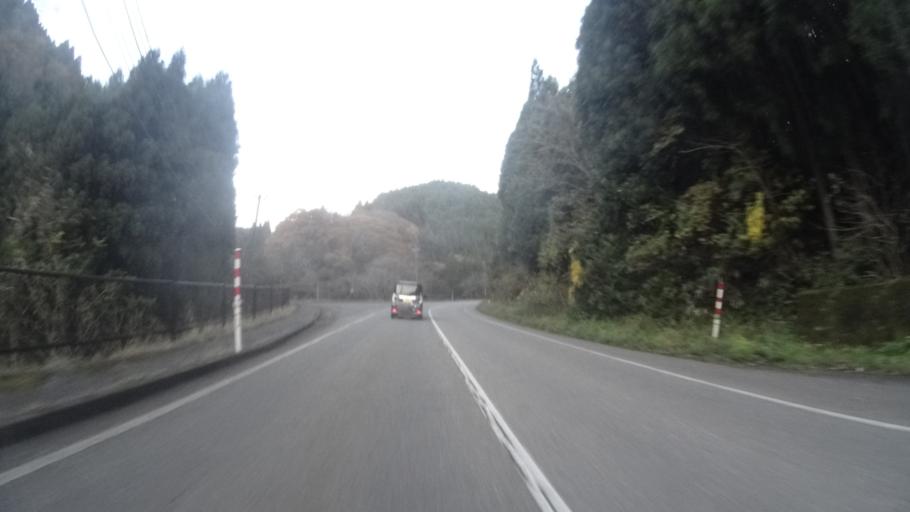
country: JP
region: Ishikawa
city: Nanao
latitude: 37.3205
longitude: 136.8100
